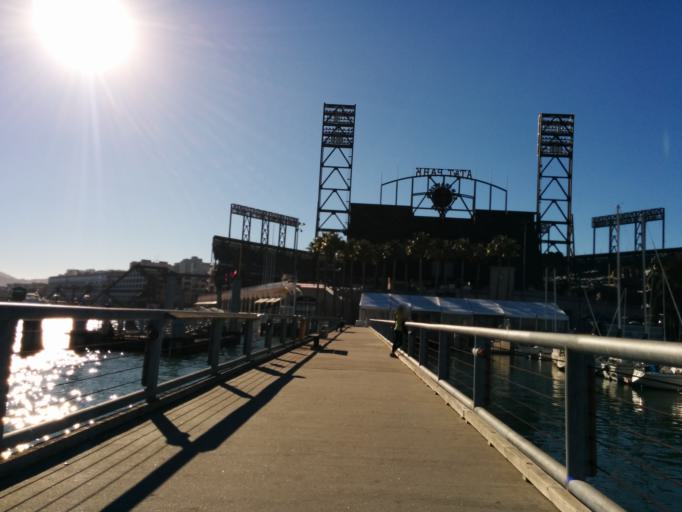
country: US
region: California
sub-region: San Francisco County
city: San Francisco
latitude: 37.7784
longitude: -122.3866
